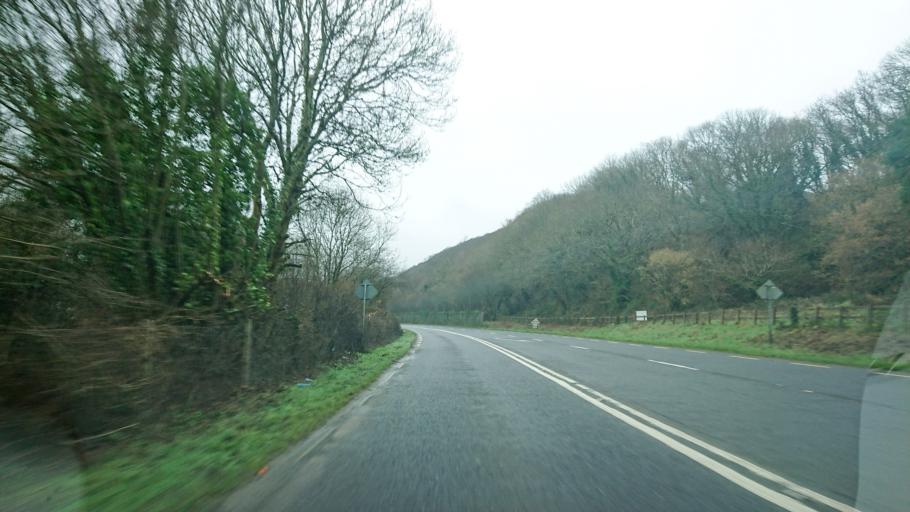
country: IE
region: Munster
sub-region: County Cork
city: Bandon
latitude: 51.7583
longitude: -8.7048
